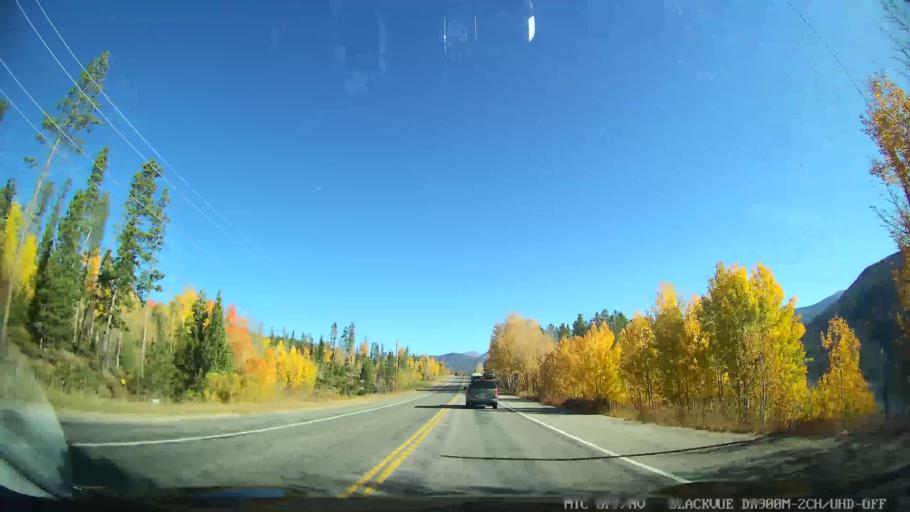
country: US
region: Colorado
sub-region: Grand County
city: Granby
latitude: 40.2292
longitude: -105.8505
